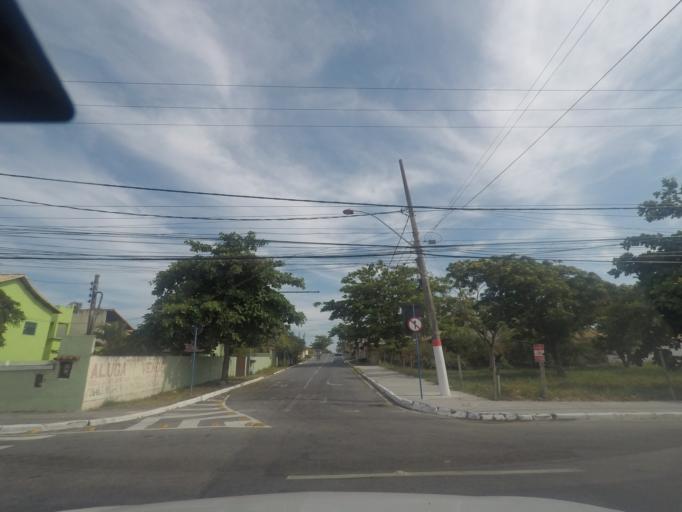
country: BR
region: Rio de Janeiro
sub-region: Marica
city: Marica
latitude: -22.9595
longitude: -42.8156
